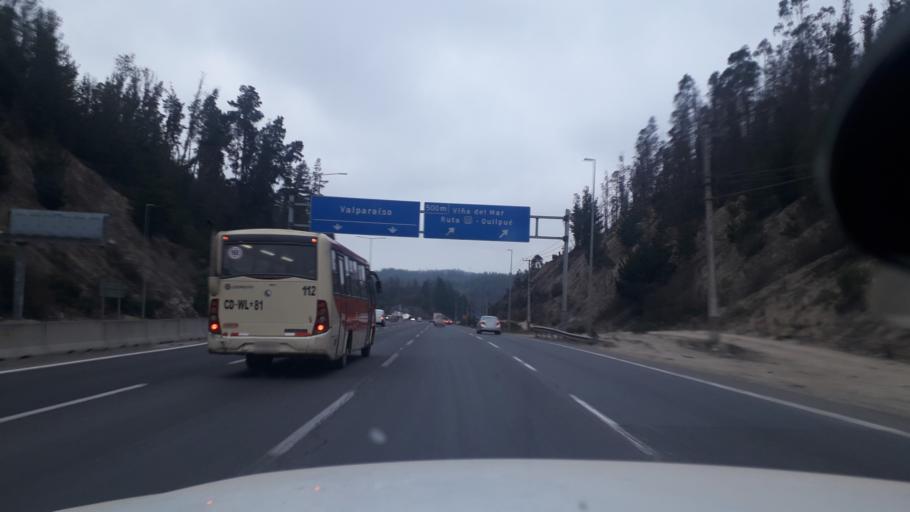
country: CL
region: Valparaiso
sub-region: Provincia de Valparaiso
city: Vina del Mar
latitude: -33.1040
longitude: -71.5480
